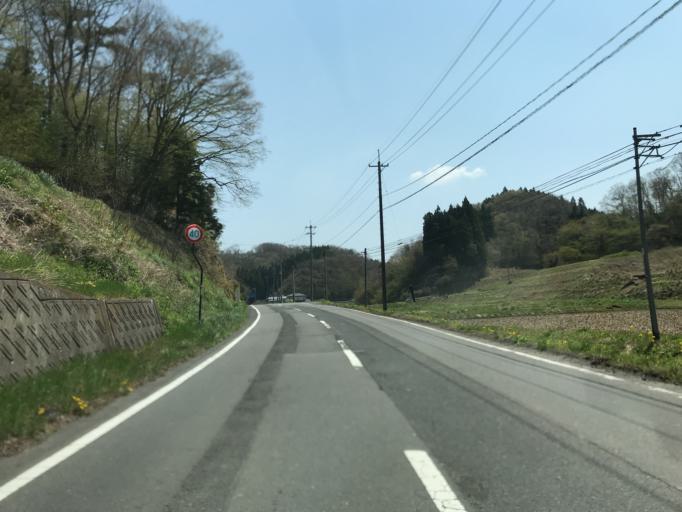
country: JP
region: Fukushima
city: Ishikawa
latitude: 37.0632
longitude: 140.4520
